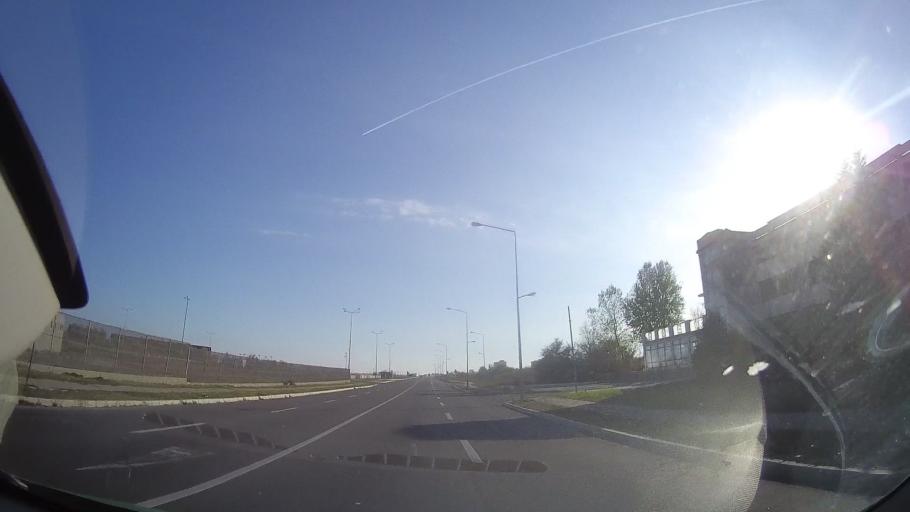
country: RO
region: Constanta
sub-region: Municipiul Mangalia
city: Mangalia
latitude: 43.8443
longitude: 28.5889
